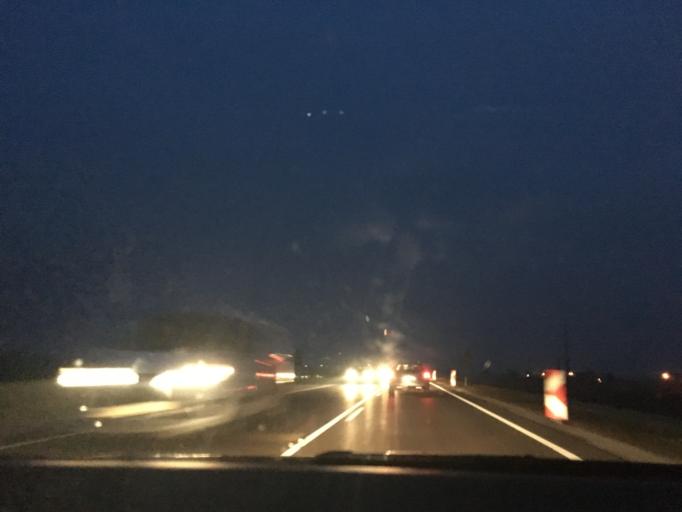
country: HU
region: Pest
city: Cegled
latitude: 47.2017
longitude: 19.7855
